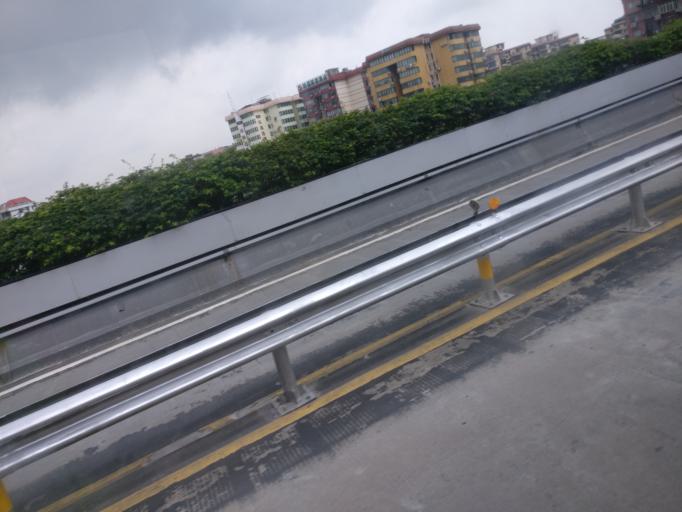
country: CN
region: Guangdong
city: Tongde
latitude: 23.1603
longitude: 113.2645
